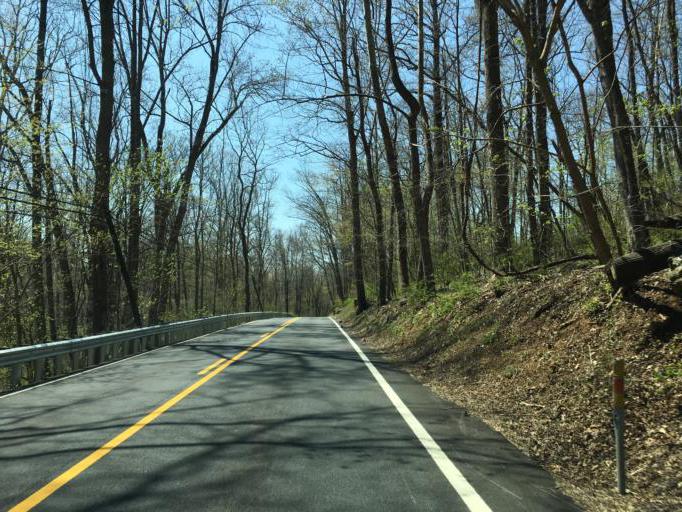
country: US
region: Maryland
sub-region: Frederick County
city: Myersville
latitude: 39.5366
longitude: -77.5317
